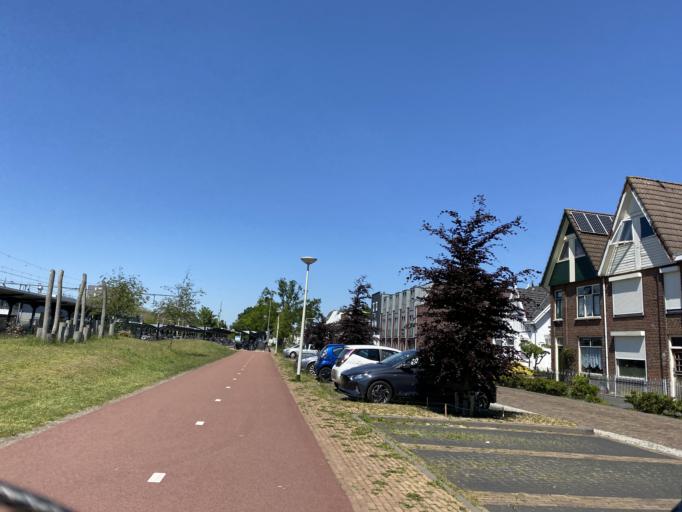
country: NL
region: North Brabant
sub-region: Gemeente Bergen op Zoom
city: Bergen op Zoom
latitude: 51.4936
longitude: 4.2964
